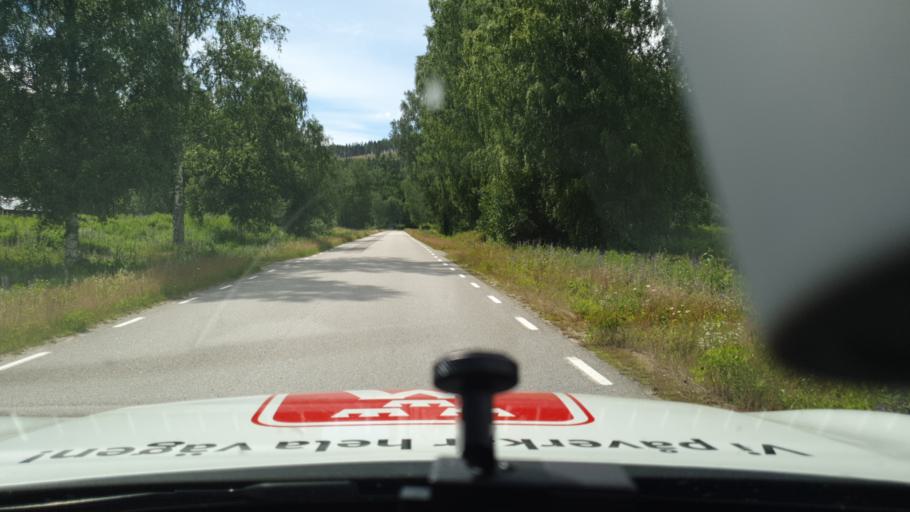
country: SE
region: Vaermland
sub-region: Hagfors Kommun
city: Ekshaerad
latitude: 60.0695
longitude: 13.4817
